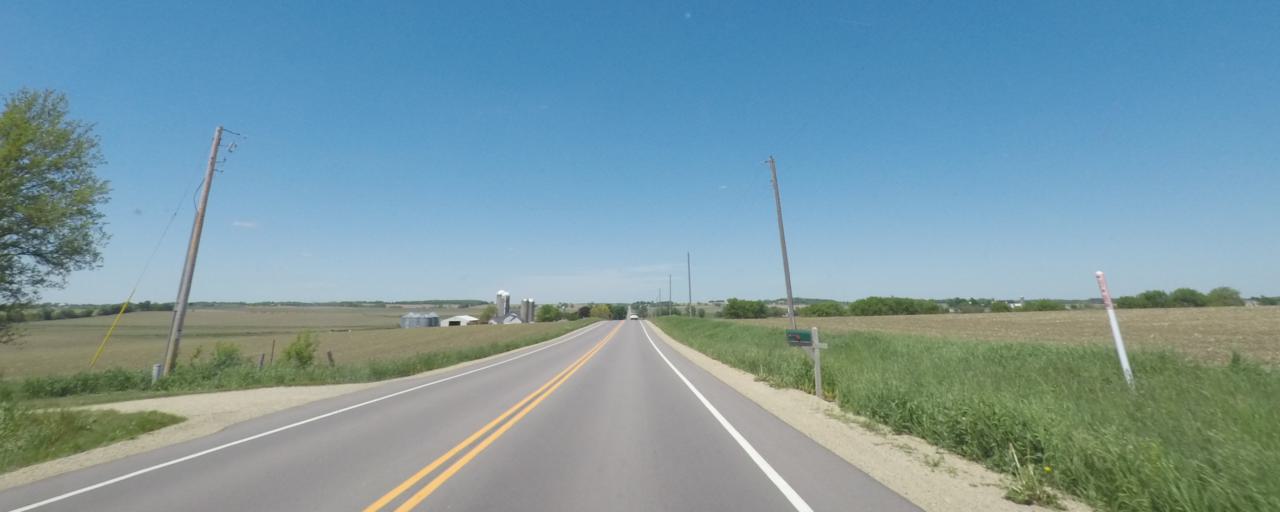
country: US
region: Wisconsin
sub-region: Green County
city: Brooklyn
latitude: 42.7916
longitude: -89.3692
